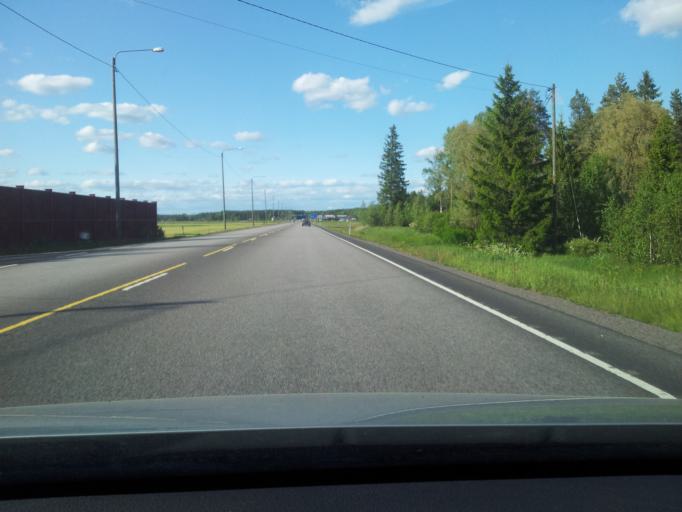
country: FI
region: Uusimaa
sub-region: Loviisa
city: Lapinjaervi
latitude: 60.6638
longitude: 26.2462
